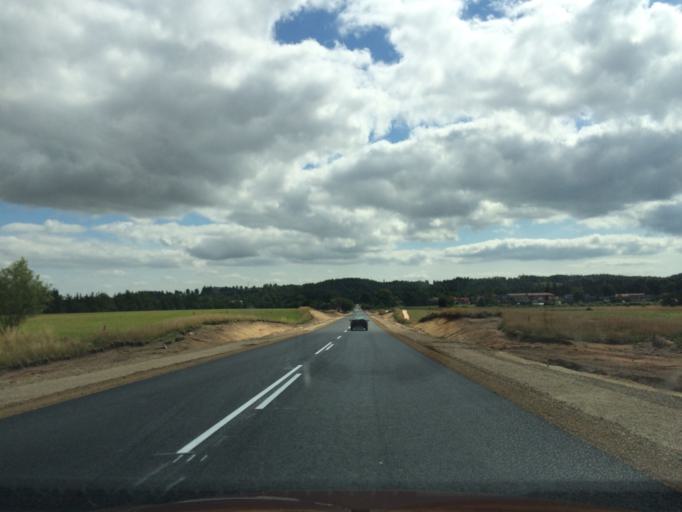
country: DK
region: Central Jutland
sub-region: Silkeborg Kommune
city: Svejbaek
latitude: 56.1858
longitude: 9.6343
